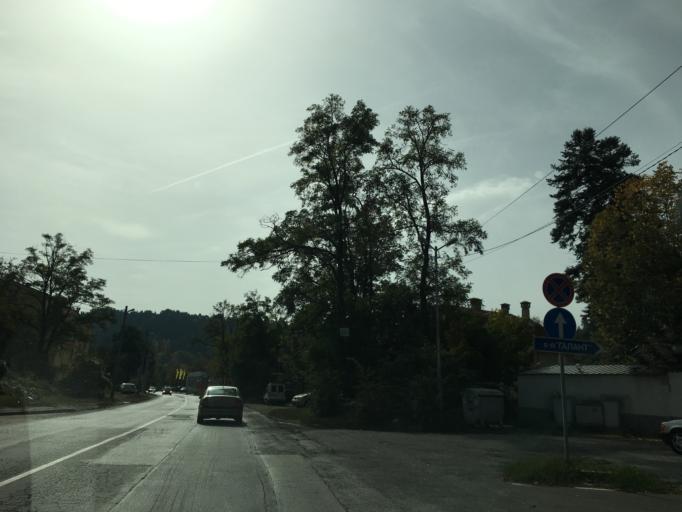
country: BG
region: Sofia-Capital
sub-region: Stolichna Obshtina
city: Sofia
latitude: 42.6119
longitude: 23.3994
